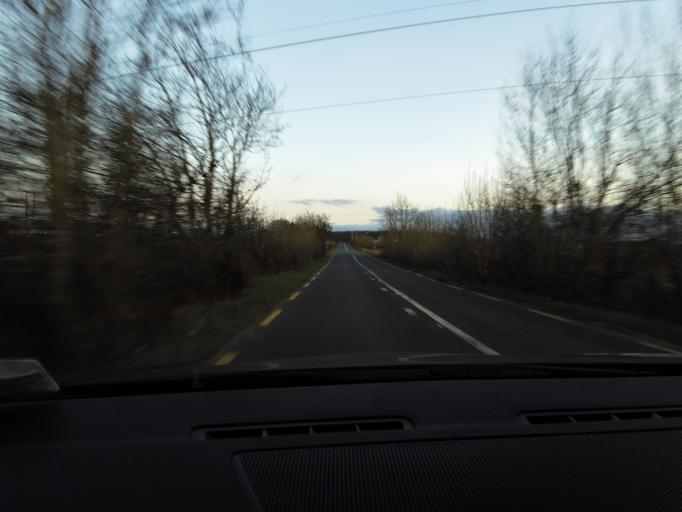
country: IE
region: Connaught
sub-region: Roscommon
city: Boyle
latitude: 53.9164
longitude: -8.2723
